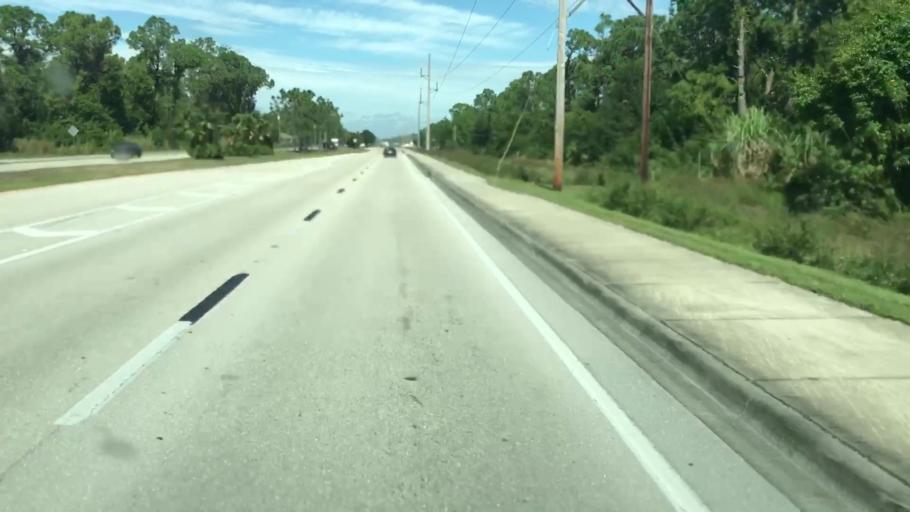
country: US
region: Florida
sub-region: Lee County
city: Gateway
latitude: 26.6098
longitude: -81.7139
